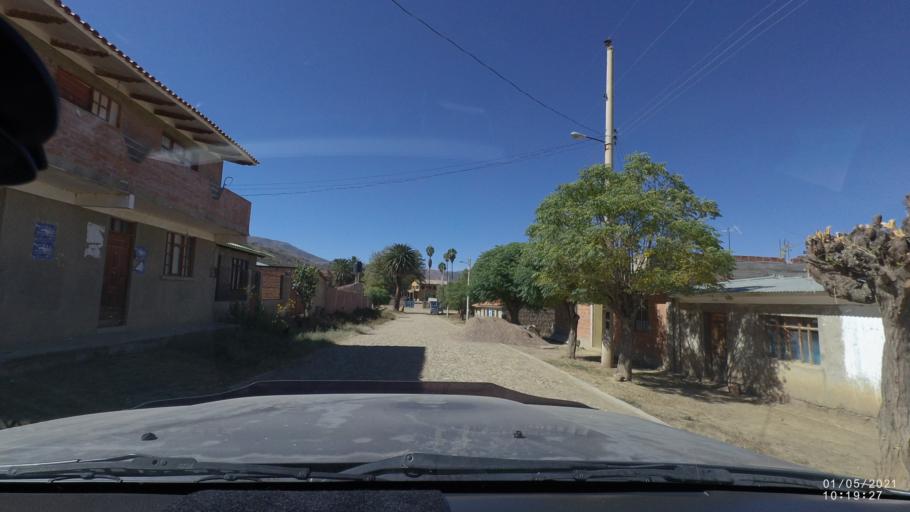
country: BO
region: Cochabamba
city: Capinota
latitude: -17.5588
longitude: -66.2058
